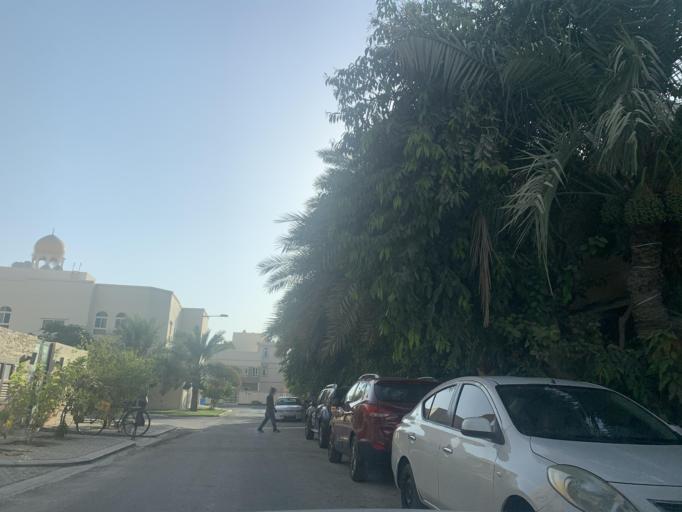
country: BH
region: Manama
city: Jidd Hafs
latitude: 26.2119
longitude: 50.5288
